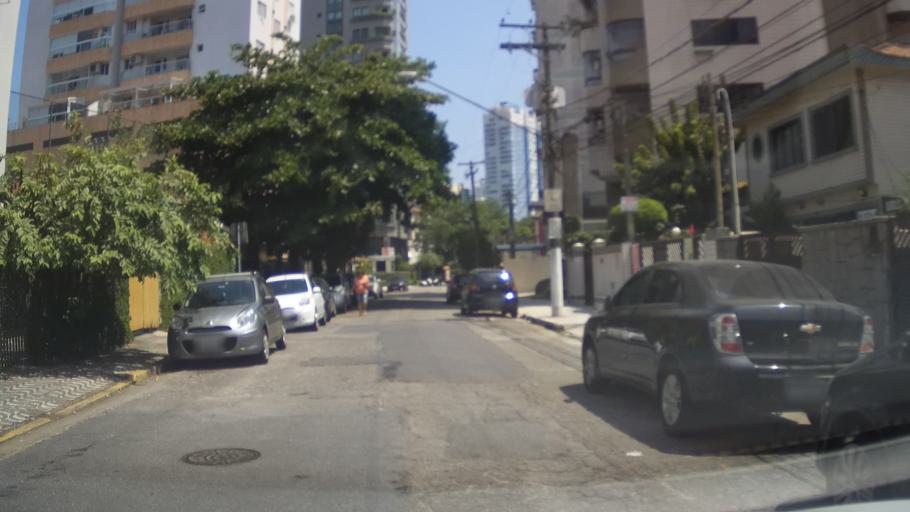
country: BR
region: Sao Paulo
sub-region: Santos
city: Santos
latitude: -23.9824
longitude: -46.3007
